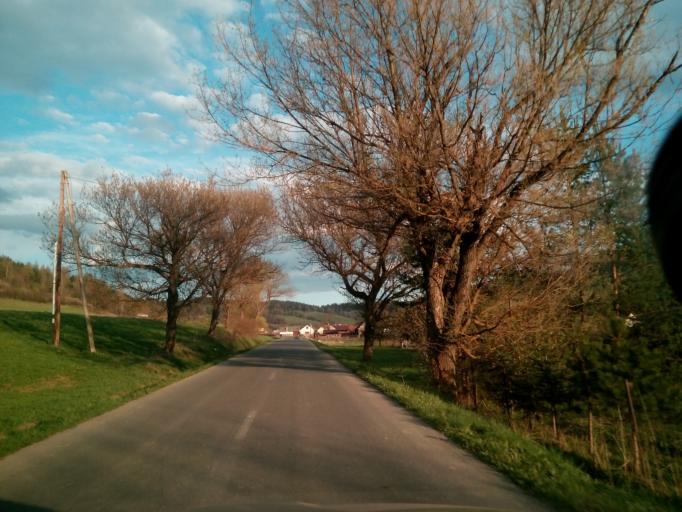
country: PL
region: Lesser Poland Voivodeship
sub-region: Powiat nowotarski
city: Niedzica
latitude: 49.3405
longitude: 20.2893
